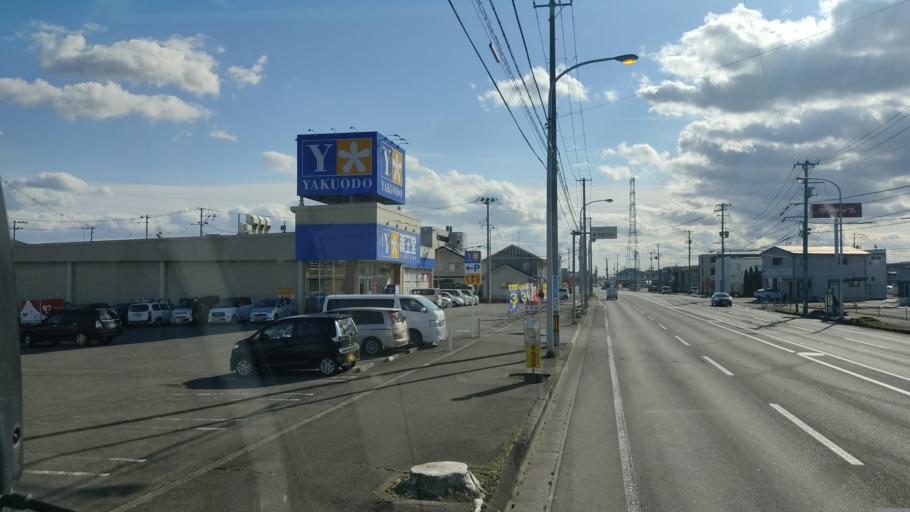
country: JP
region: Iwate
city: Morioka-shi
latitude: 39.6819
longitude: 141.1433
